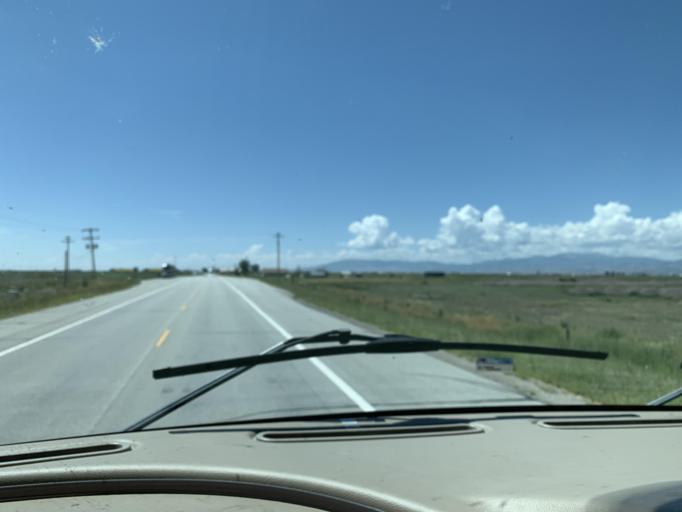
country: US
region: Colorado
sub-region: Saguache County
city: Center
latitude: 37.8627
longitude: -106.1464
